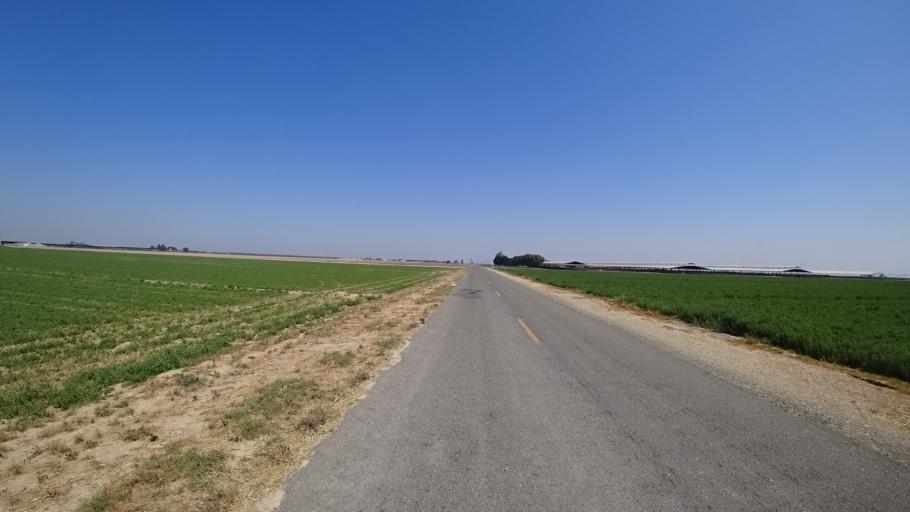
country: US
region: California
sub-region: Tulare County
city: Goshen
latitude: 36.3923
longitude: -119.5289
